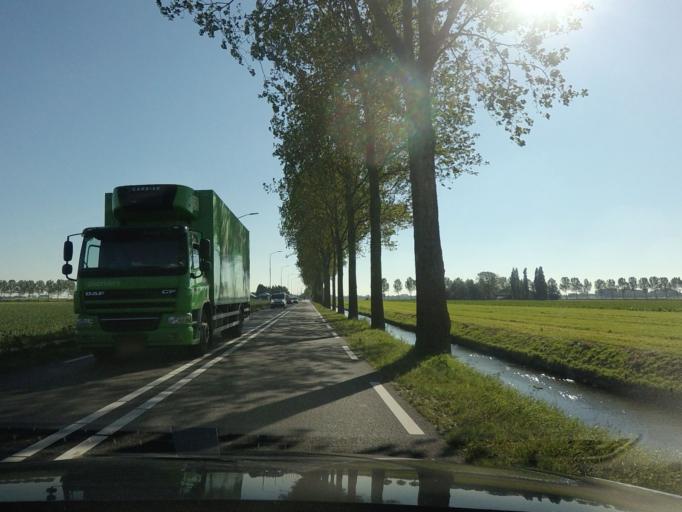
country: NL
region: North Holland
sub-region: Gemeente Haarlemmermeer
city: Hoofddorp
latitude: 52.2755
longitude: 4.6813
